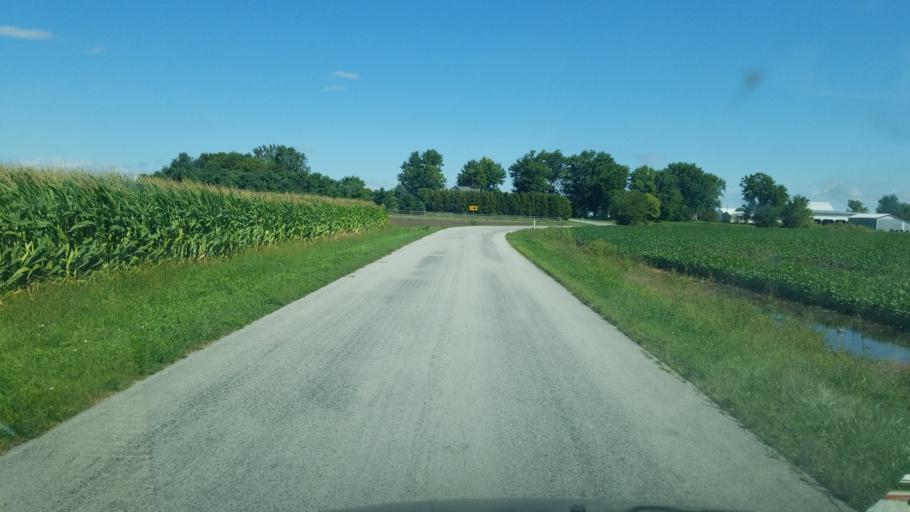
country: US
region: Ohio
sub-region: Hancock County
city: McComb
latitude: 41.1382
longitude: -83.7461
